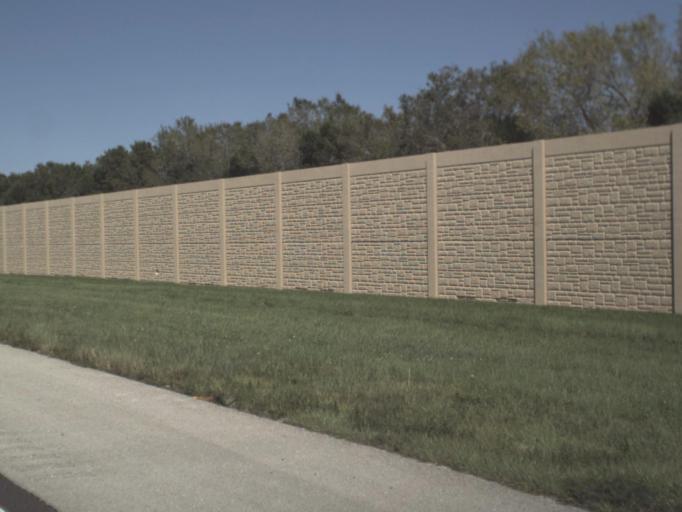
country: US
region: Florida
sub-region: Lee County
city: Bonita Springs
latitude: 26.3172
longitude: -81.7463
